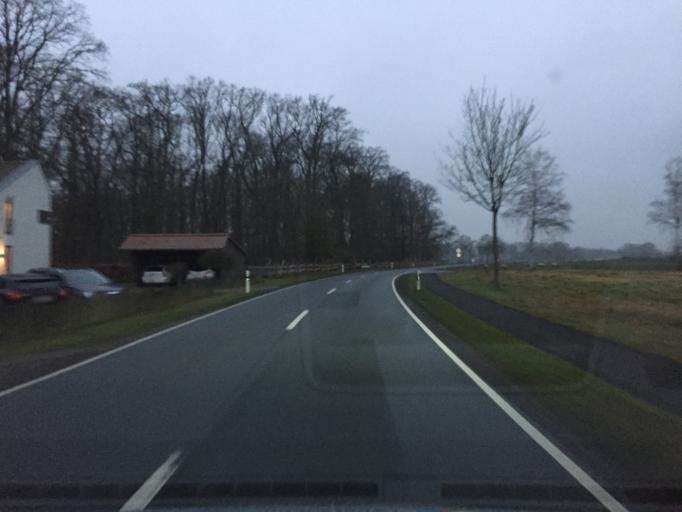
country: DE
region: Lower Saxony
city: Borstel
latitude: 52.5996
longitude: 8.9474
